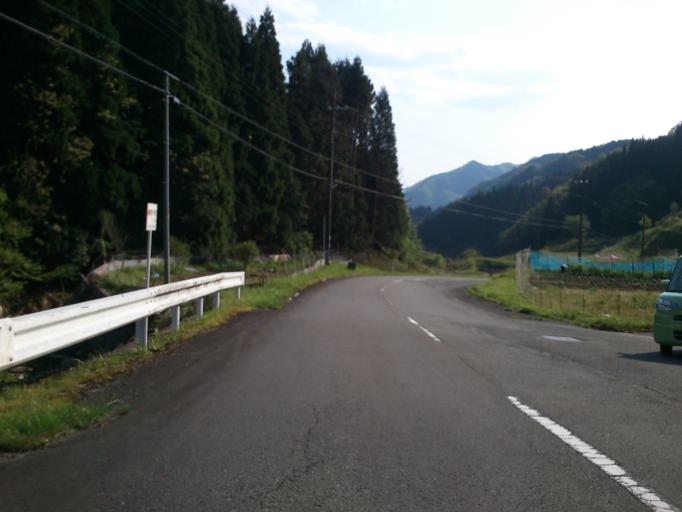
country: JP
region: Kyoto
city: Fukuchiyama
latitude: 35.3620
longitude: 135.0216
